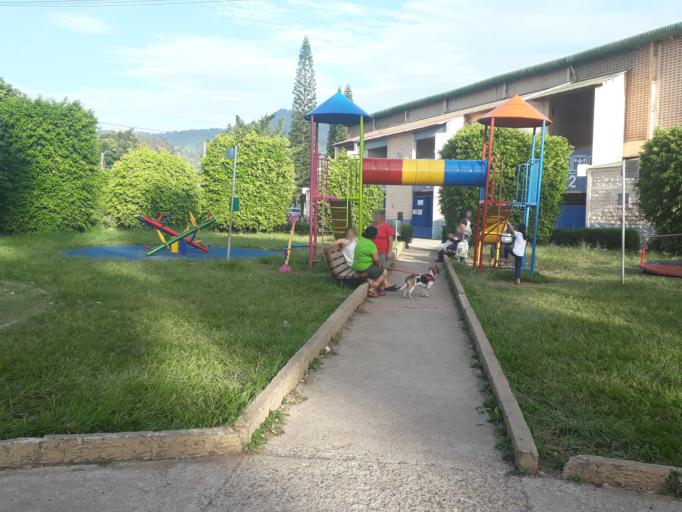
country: HN
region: Francisco Morazan
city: Tegucigalpa
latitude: 14.0906
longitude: -87.1634
